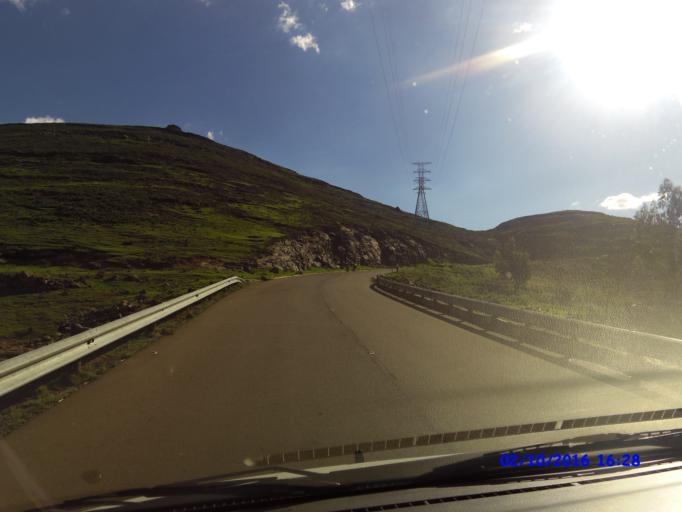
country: LS
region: Maseru
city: Nako
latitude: -29.4748
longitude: 28.0879
